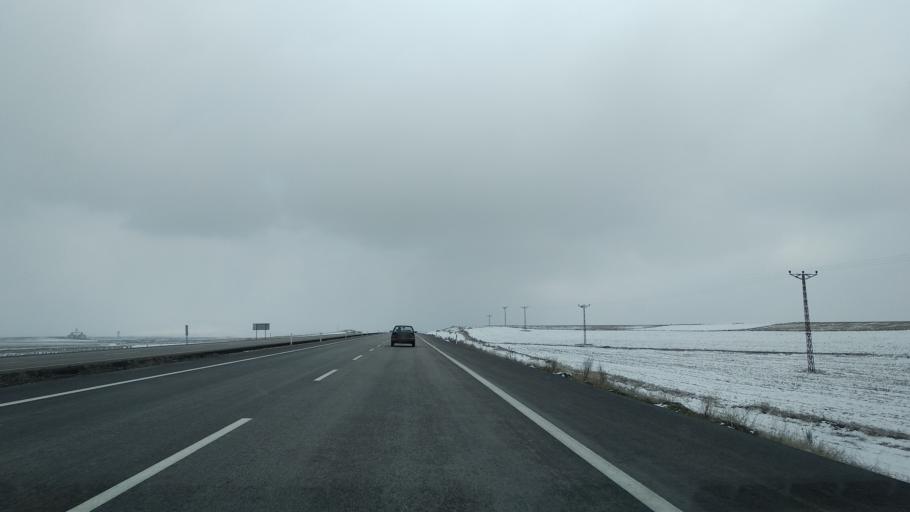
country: TR
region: Kayseri
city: Elbasi
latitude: 38.6526
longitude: 36.0024
